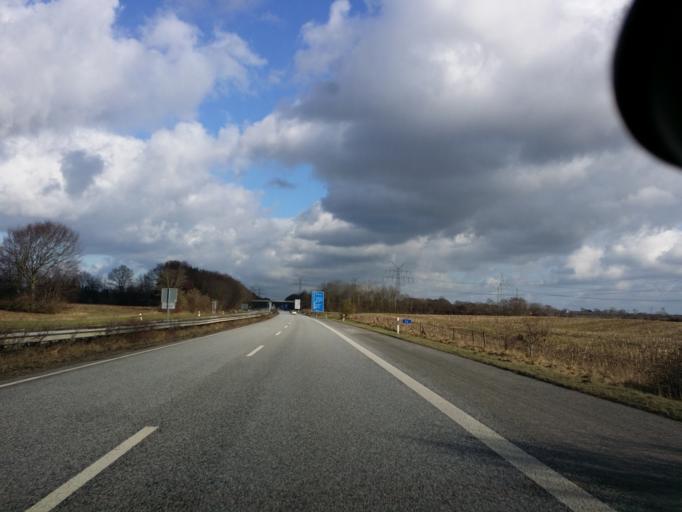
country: DE
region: Schleswig-Holstein
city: Schulldorf
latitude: 54.2964
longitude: 9.7286
